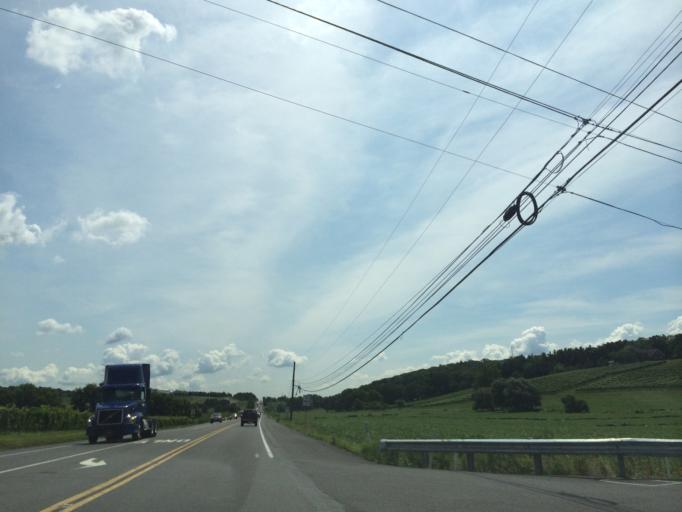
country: US
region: Pennsylvania
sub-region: Lehigh County
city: Breinigsville
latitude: 40.5444
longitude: -75.6722
